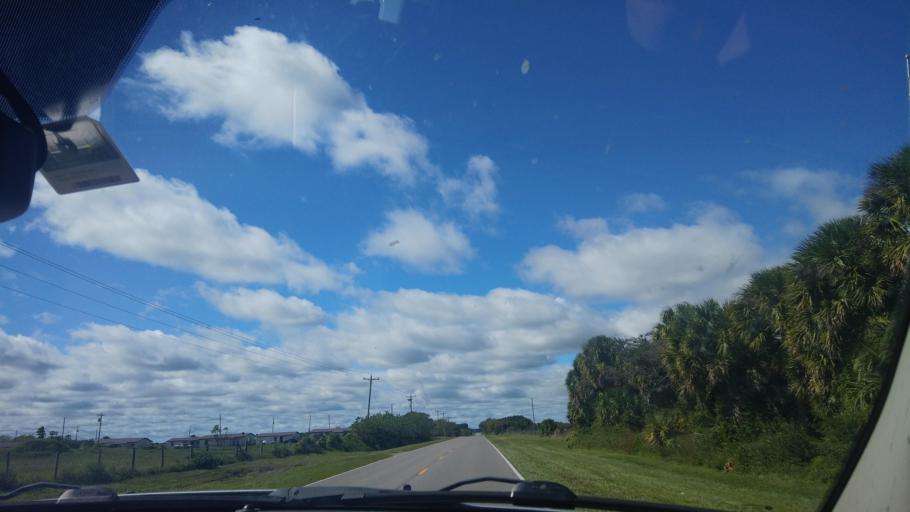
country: US
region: Florida
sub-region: Okeechobee County
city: Cypress Quarters
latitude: 27.3905
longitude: -80.8239
